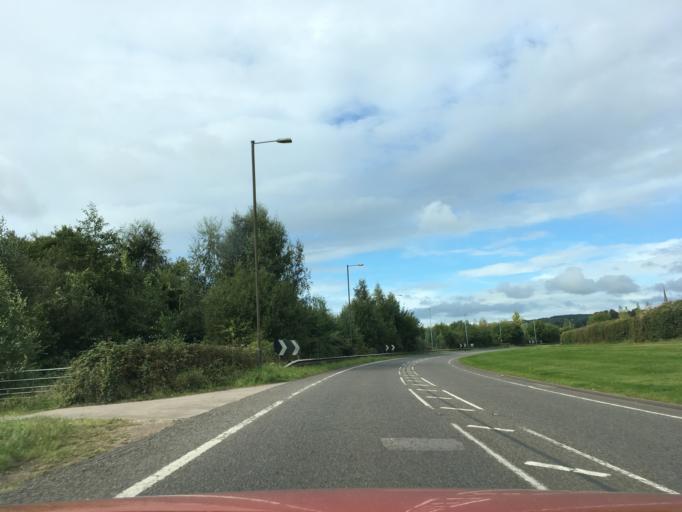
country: GB
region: England
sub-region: Gloucestershire
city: Lydney
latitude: 51.7172
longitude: -2.5225
